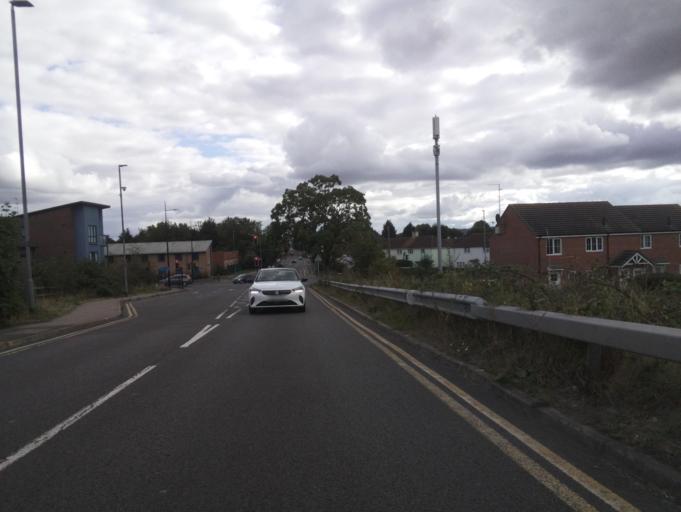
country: GB
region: England
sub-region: Leicestershire
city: Loughborough
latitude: 52.7819
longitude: -1.2016
